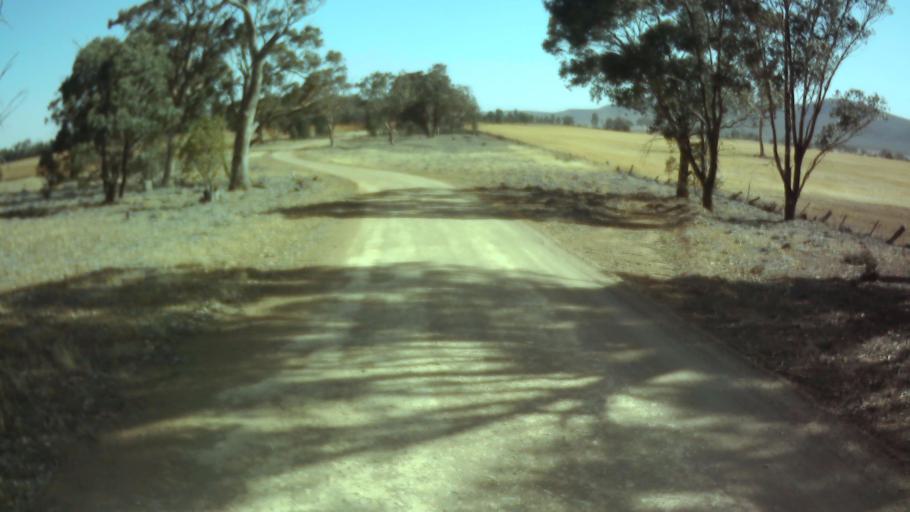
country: AU
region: New South Wales
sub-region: Weddin
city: Grenfell
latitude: -33.8556
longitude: 148.0156
